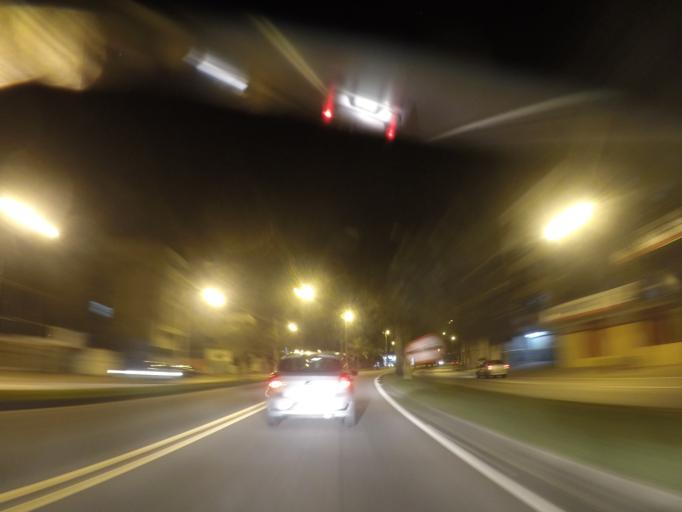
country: BR
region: Espirito Santo
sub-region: Linhares
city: Linhares
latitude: -19.4022
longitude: -40.0610
